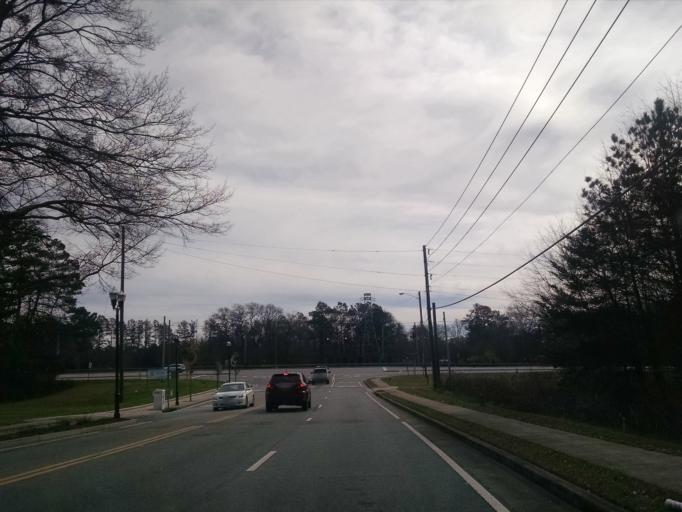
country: US
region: Georgia
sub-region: Gwinnett County
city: Sugar Hill
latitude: 34.1051
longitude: -84.0321
